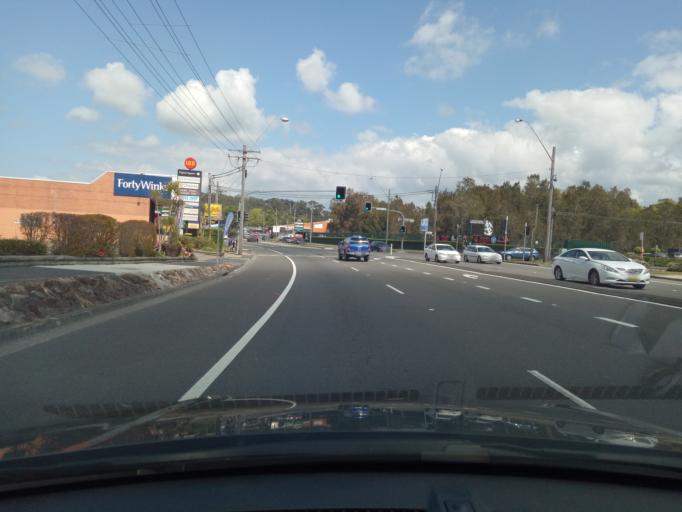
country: AU
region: New South Wales
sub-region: Gosford Shire
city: Erina
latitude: -33.4356
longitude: 151.3856
